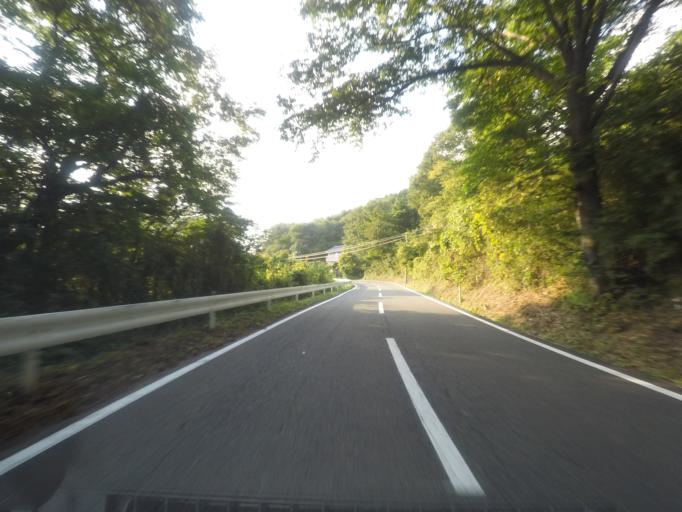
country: JP
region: Fukushima
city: Funehikimachi-funehiki
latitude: 37.5558
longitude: 140.7774
